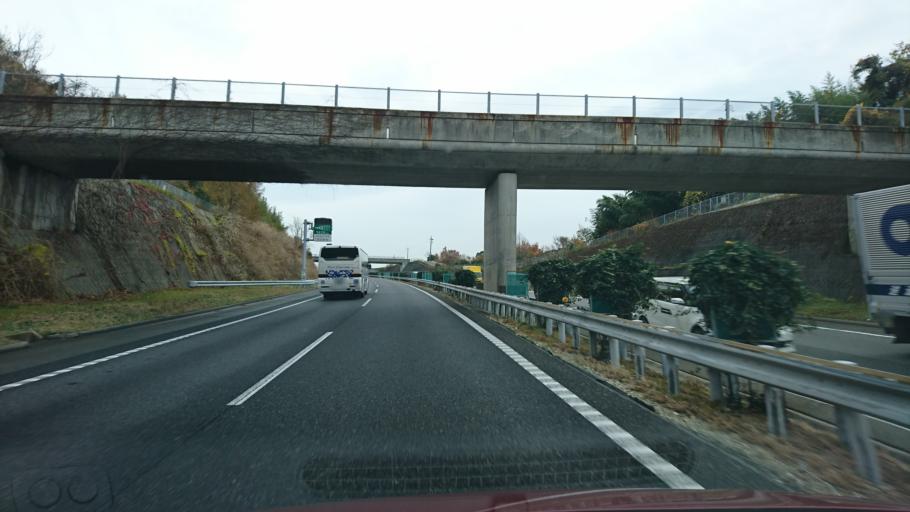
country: JP
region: Hyogo
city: Sandacho
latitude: 34.8207
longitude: 135.1366
